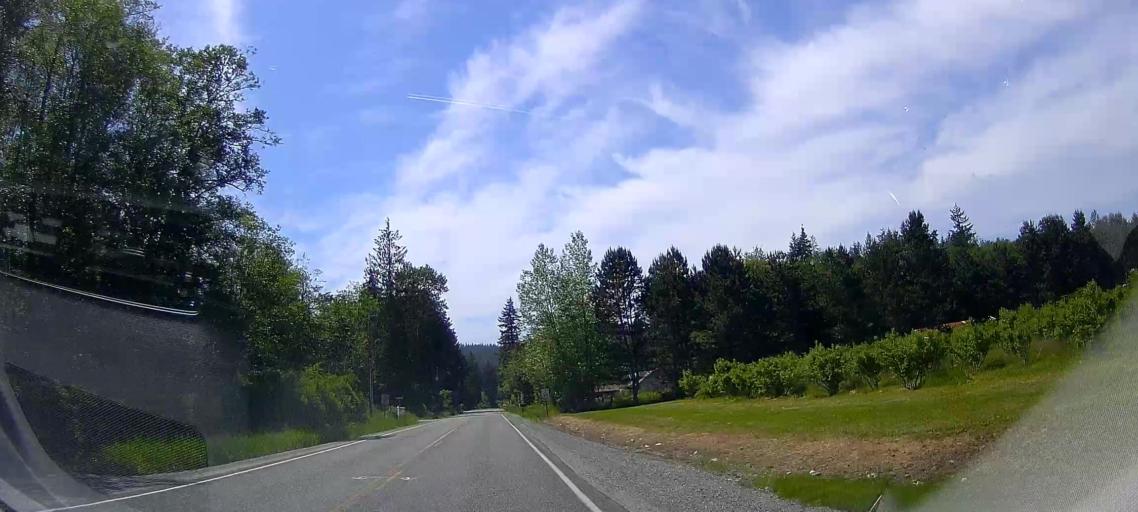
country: US
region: Washington
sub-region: Skagit County
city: Big Lake
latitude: 48.3949
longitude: -122.2749
